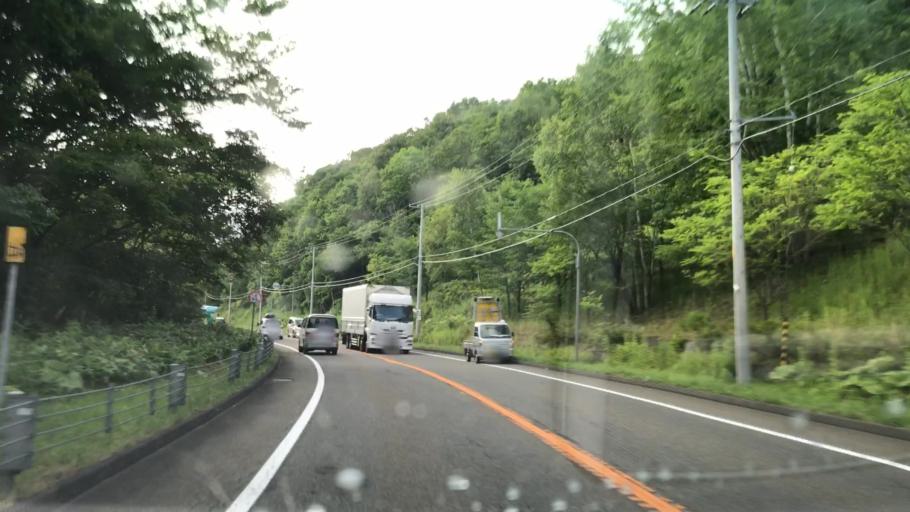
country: JP
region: Hokkaido
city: Shimo-furano
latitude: 42.8919
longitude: 142.2484
